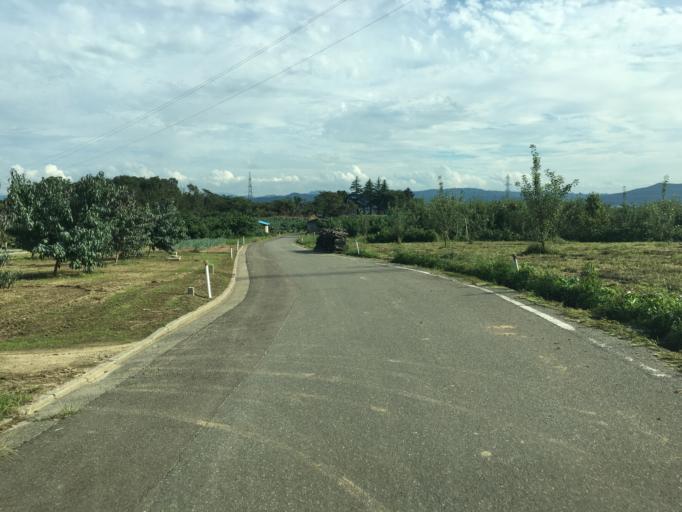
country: JP
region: Fukushima
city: Hobaramachi
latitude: 37.8326
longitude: 140.4725
